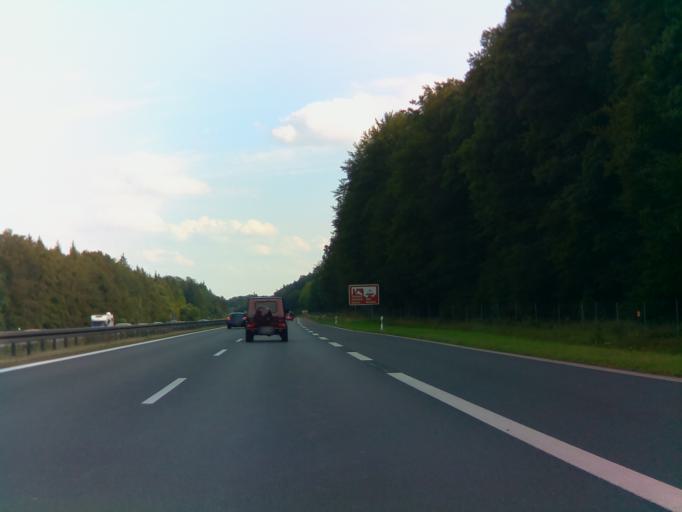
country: DE
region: Bavaria
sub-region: Regierungsbezirk Unterfranken
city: Schondra
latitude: 50.2270
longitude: 9.8948
